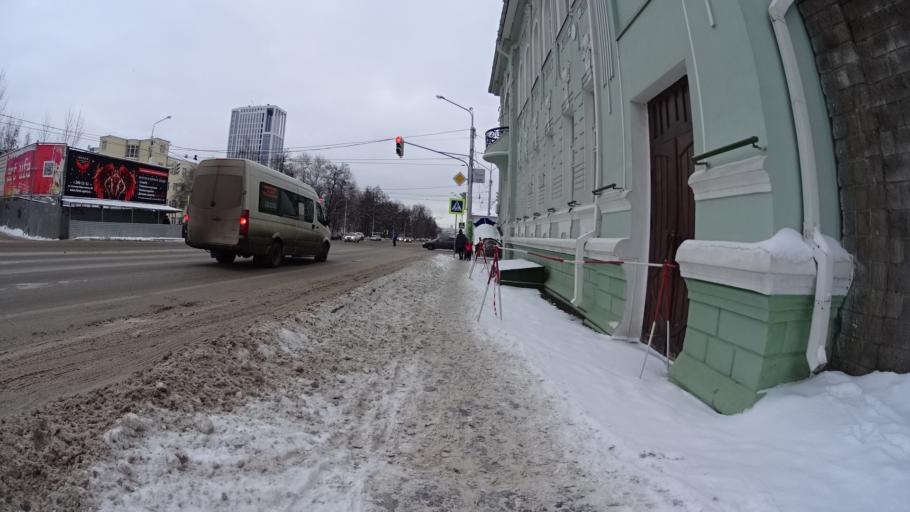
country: RU
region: Bashkortostan
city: Ufa
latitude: 54.7229
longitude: 55.9388
